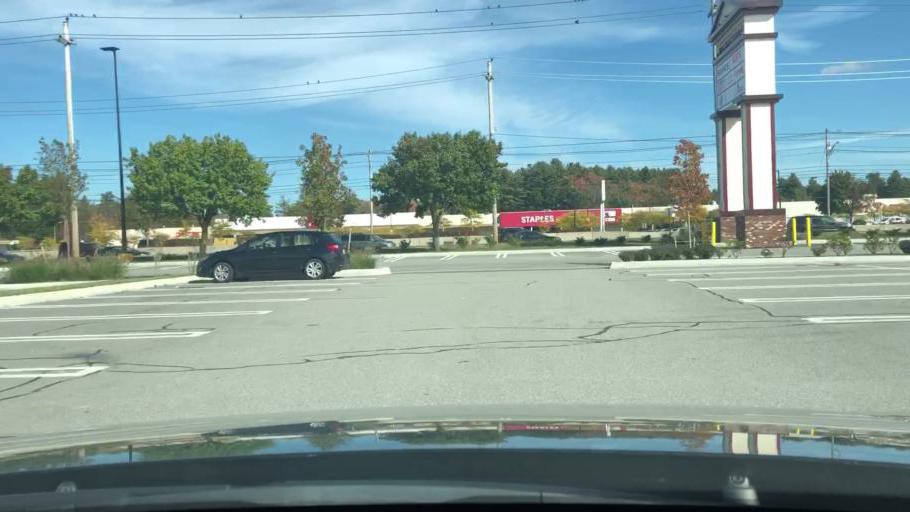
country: US
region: New Hampshire
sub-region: Rockingham County
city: Salem
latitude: 42.7672
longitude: -71.2200
